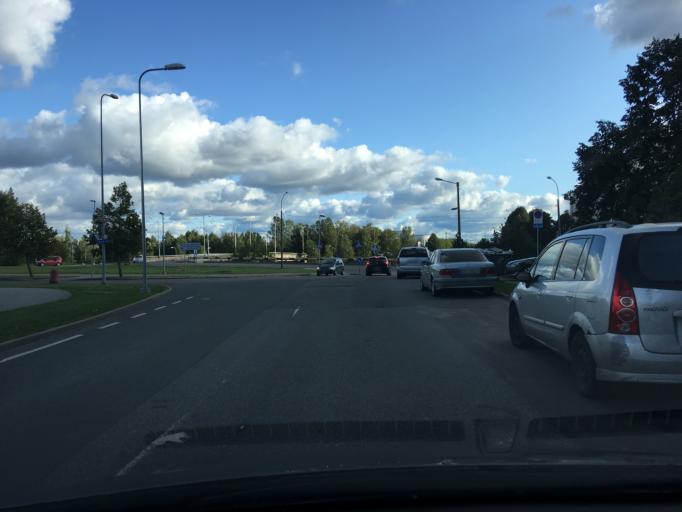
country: EE
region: Harju
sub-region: Tallinna linn
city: Kose
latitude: 59.4414
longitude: 24.8488
